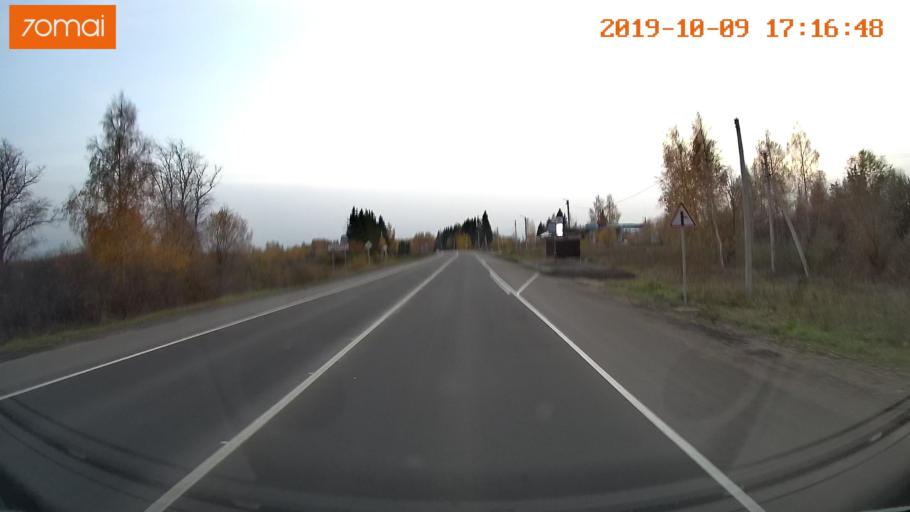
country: RU
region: Ivanovo
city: Furmanov
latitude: 57.2843
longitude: 41.1612
